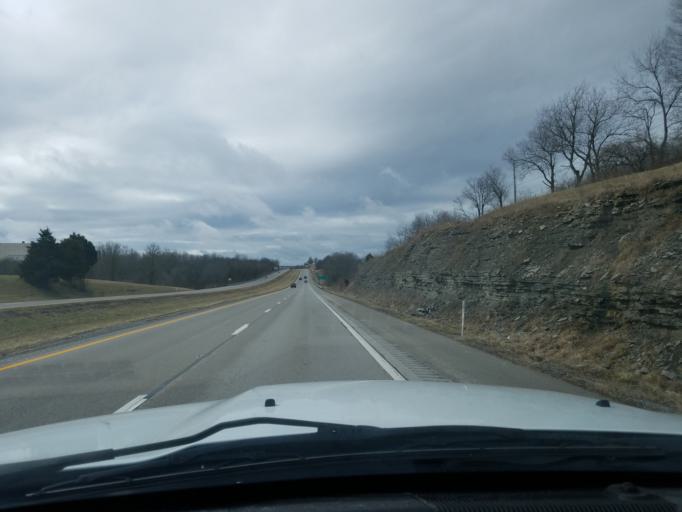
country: US
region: Kentucky
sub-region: Montgomery County
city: Mount Sterling
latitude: 38.0869
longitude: -83.9131
